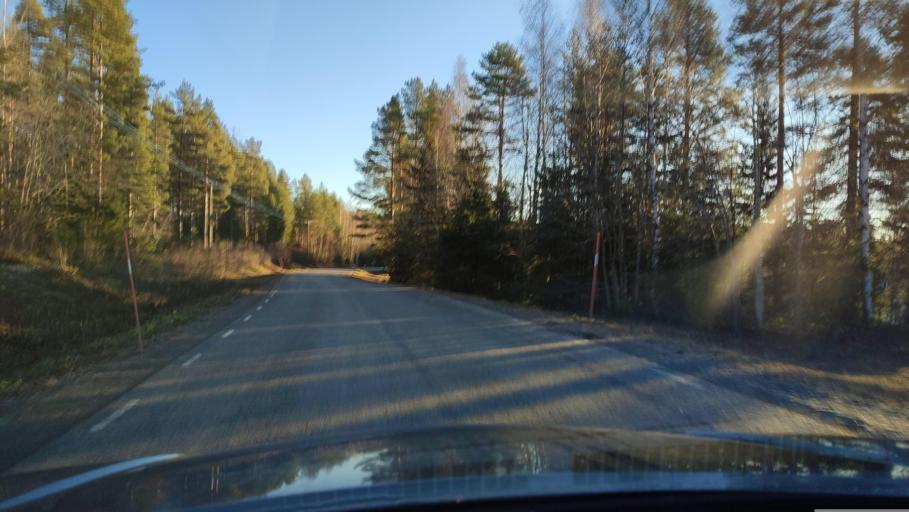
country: SE
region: Vaesterbotten
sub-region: Skelleftea Kommun
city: Viken
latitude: 64.6963
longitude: 20.9211
